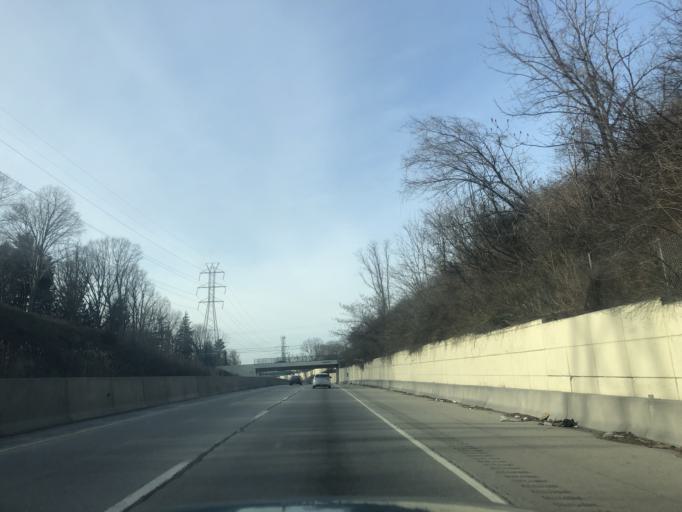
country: US
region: Pennsylvania
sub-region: Montgomery County
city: Wyndmoor
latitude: 40.0979
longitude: -75.1777
